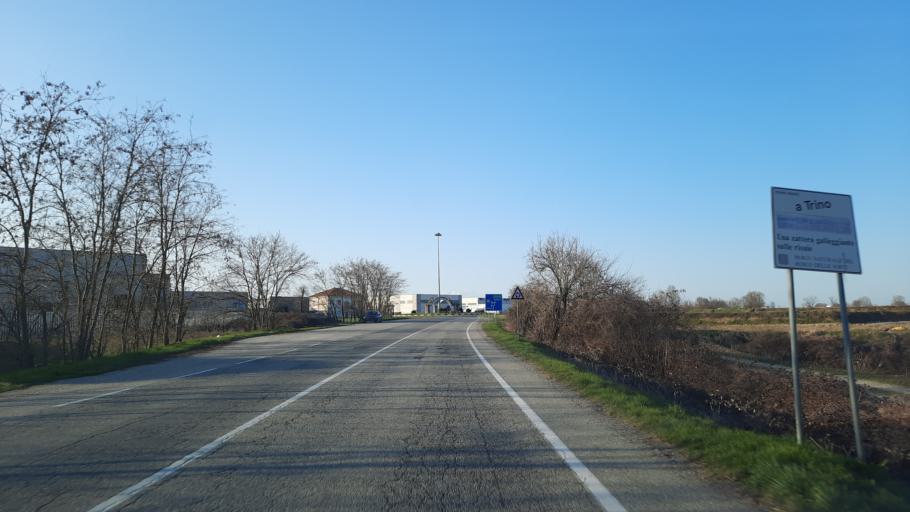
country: IT
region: Piedmont
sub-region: Provincia di Vercelli
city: Trino
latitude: 45.2062
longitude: 8.3050
